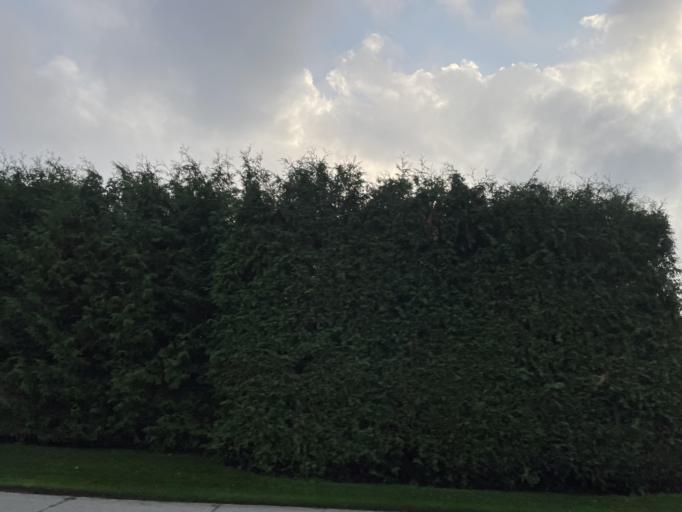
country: CA
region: Ontario
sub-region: Wellington County
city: Guelph
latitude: 43.5221
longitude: -80.2808
